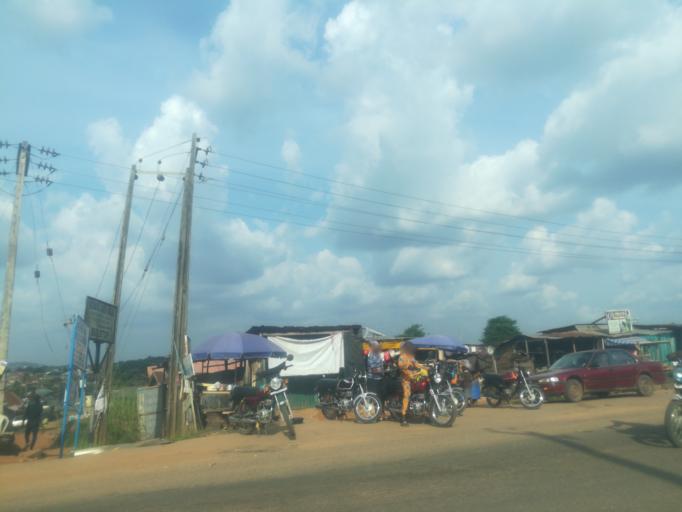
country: NG
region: Oyo
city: Ido
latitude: 7.3972
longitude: 3.8079
